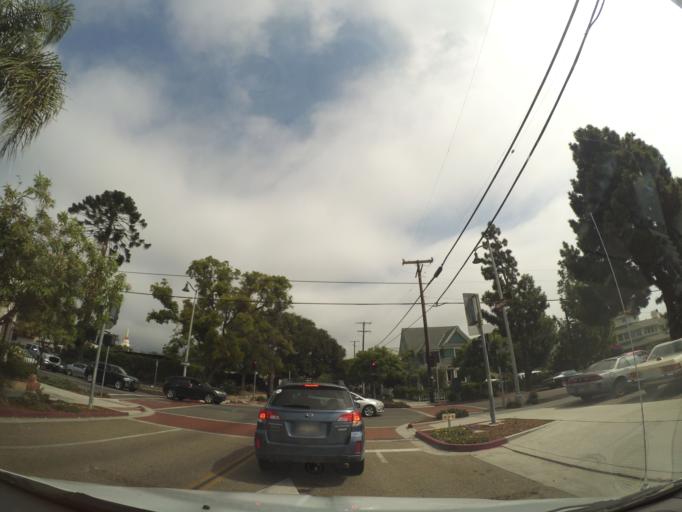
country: US
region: California
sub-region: Santa Barbara County
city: Santa Barbara
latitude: 34.4211
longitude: -119.7069
